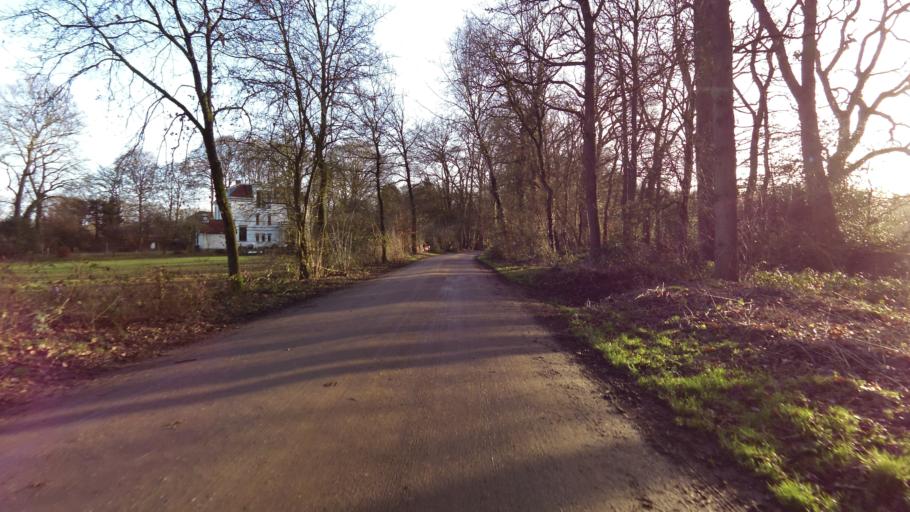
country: NL
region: Gelderland
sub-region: Gemeente Epe
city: Vaassen
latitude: 52.2549
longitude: 5.9220
